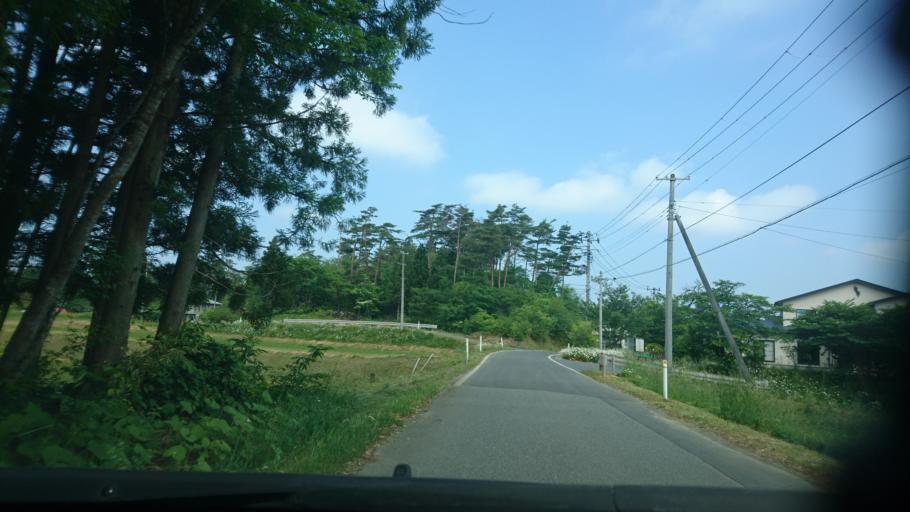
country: JP
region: Iwate
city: Ichinoseki
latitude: 38.9022
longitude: 141.2400
